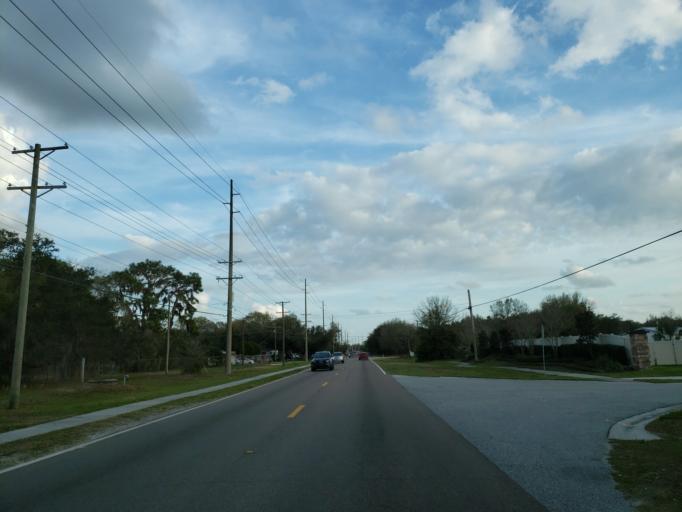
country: US
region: Florida
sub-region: Hillsborough County
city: Riverview
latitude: 27.8271
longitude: -82.3022
